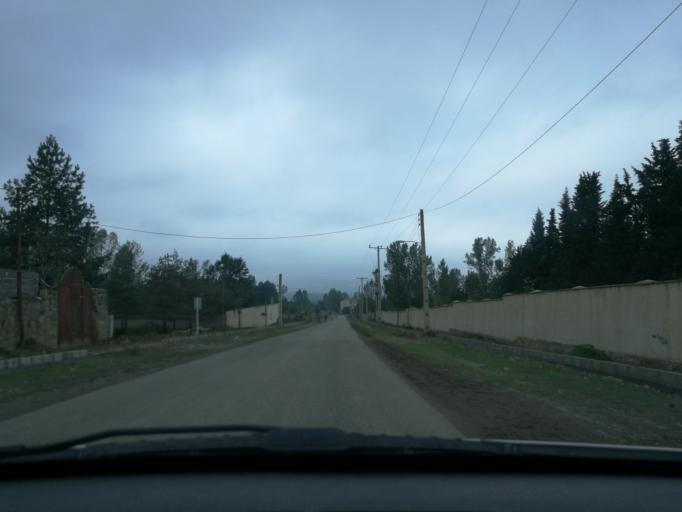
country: IR
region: Mazandaran
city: `Abbasabad
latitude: 36.4988
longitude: 51.2159
